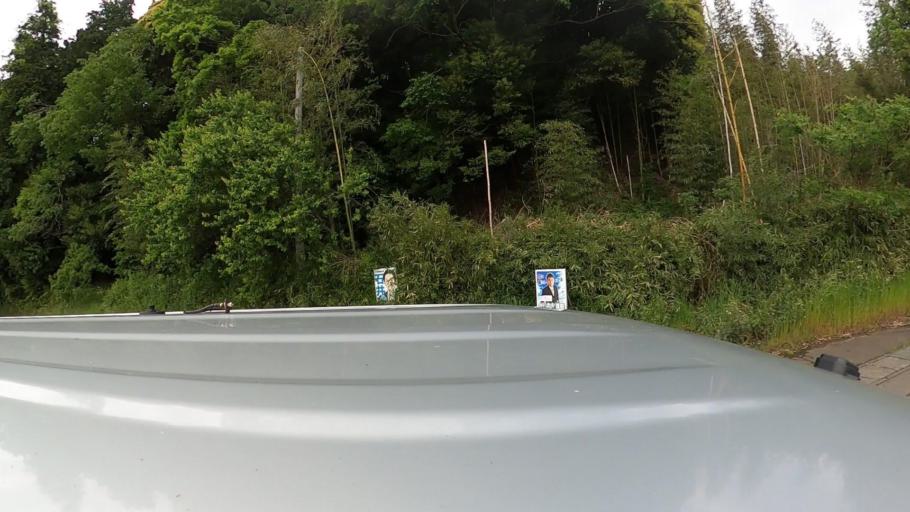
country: JP
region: Ibaraki
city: Ryugasaki
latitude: 35.9648
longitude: 140.2013
